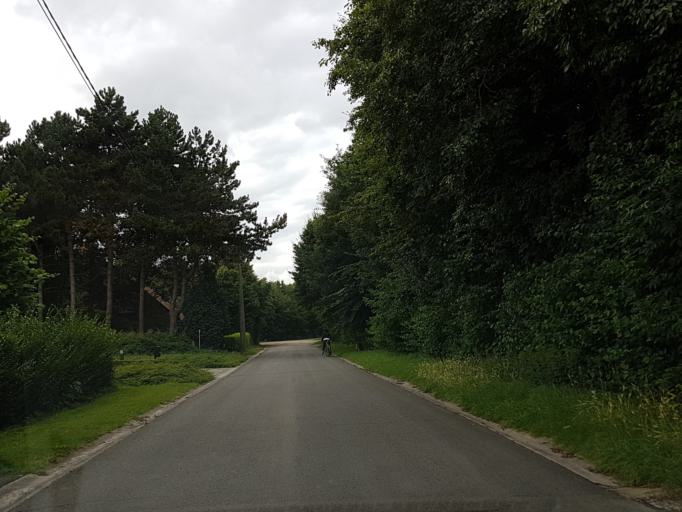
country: BE
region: Flanders
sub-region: Provincie Vlaams-Brabant
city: Machelen
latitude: 50.9136
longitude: 4.4673
